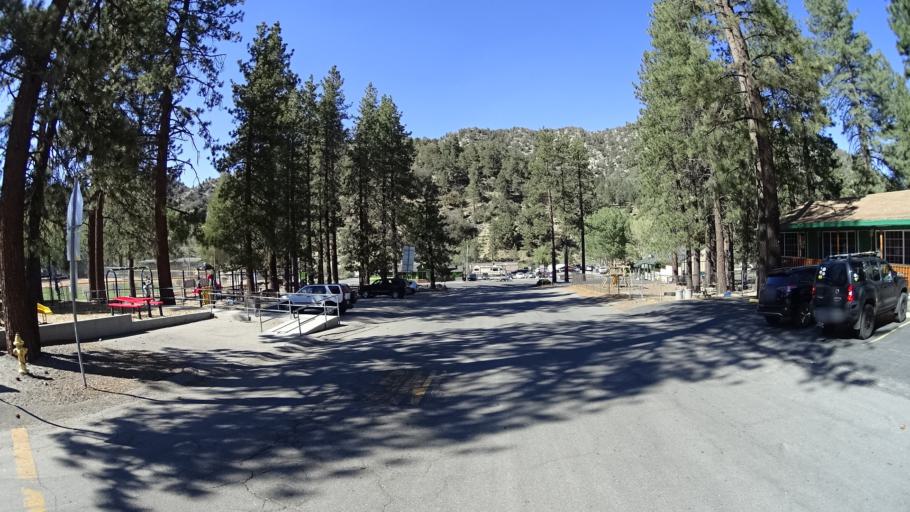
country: US
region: California
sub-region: San Bernardino County
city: Wrightwood
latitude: 34.3608
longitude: -117.6349
